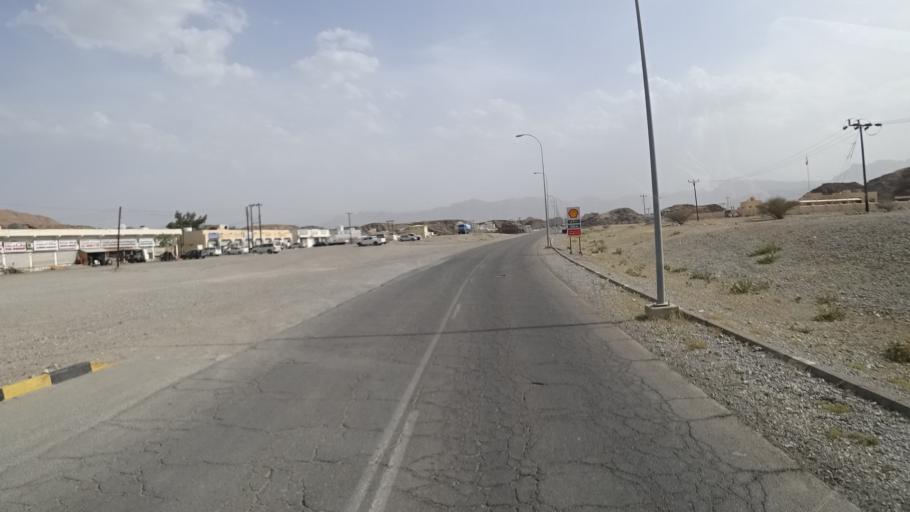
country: OM
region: Muhafazat Masqat
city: Bawshar
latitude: 23.3865
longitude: 58.5131
